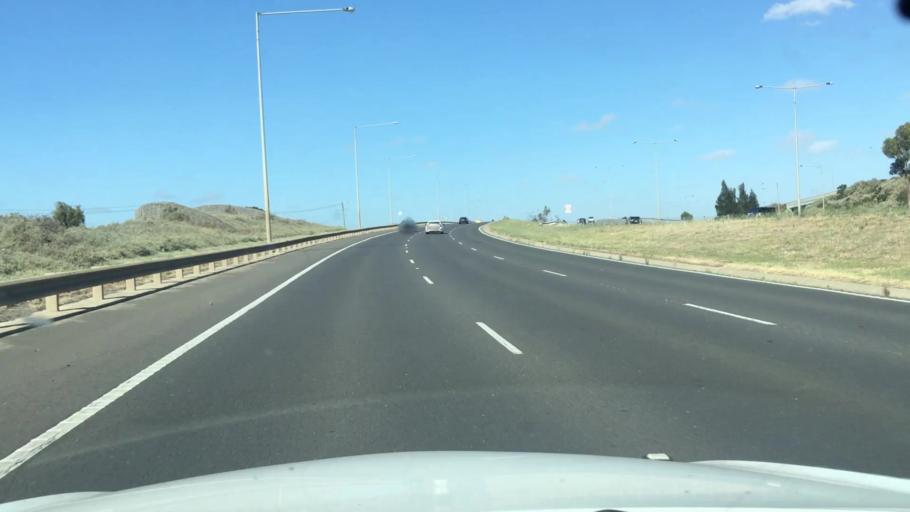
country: AU
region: Victoria
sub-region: Greater Geelong
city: Lara
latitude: -38.0557
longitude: 144.3931
